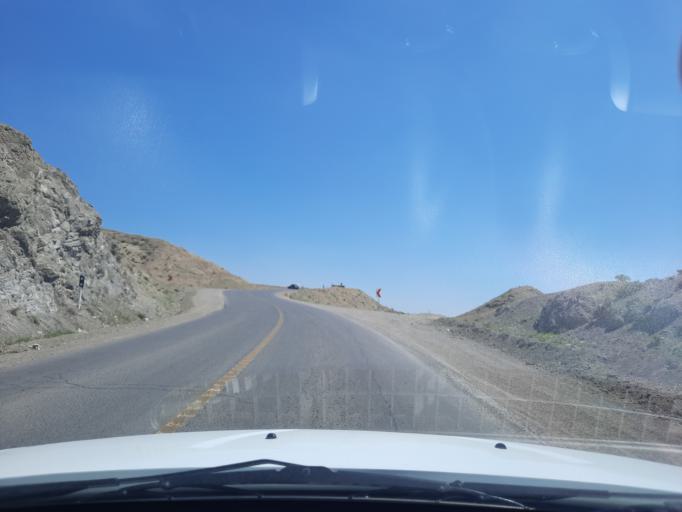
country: IR
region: Qazvin
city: Qazvin
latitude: 36.3560
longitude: 50.1887
